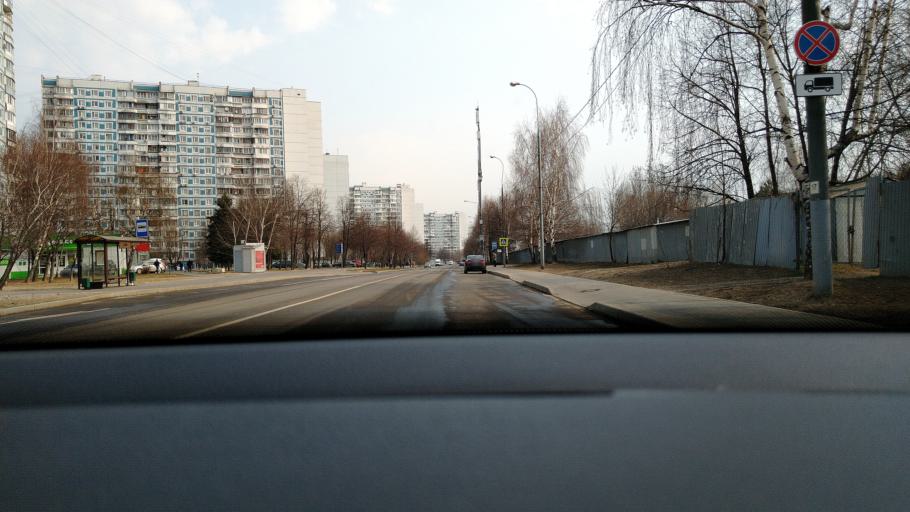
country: RU
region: Moskovskaya
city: Razvilka
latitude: 55.6039
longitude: 37.7484
